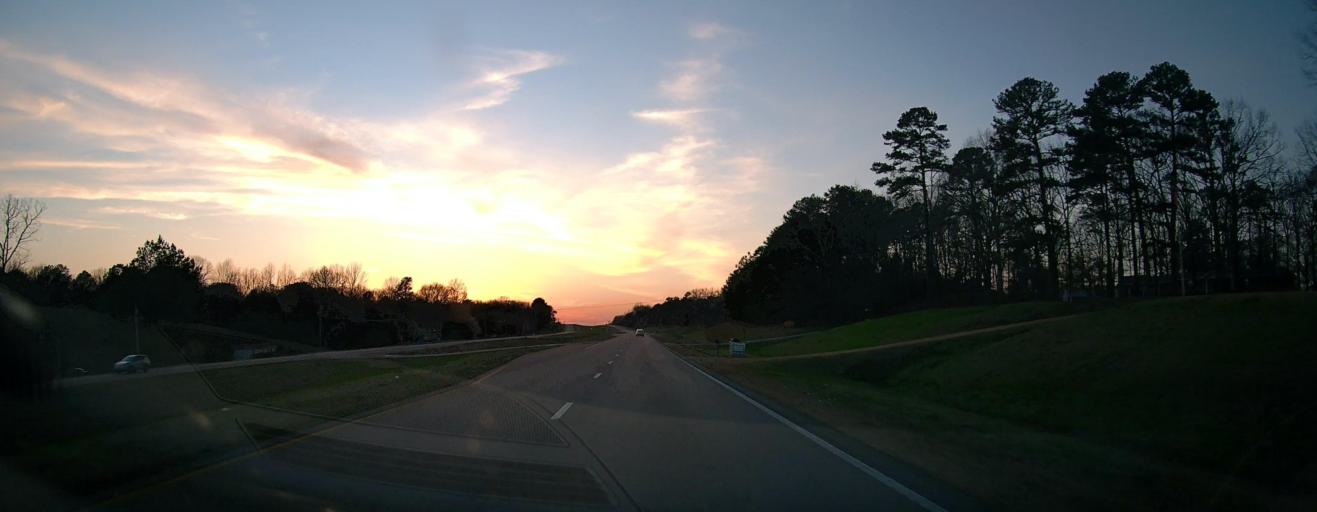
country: US
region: Mississippi
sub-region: Tippah County
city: Ripley
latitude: 34.9518
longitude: -88.8297
